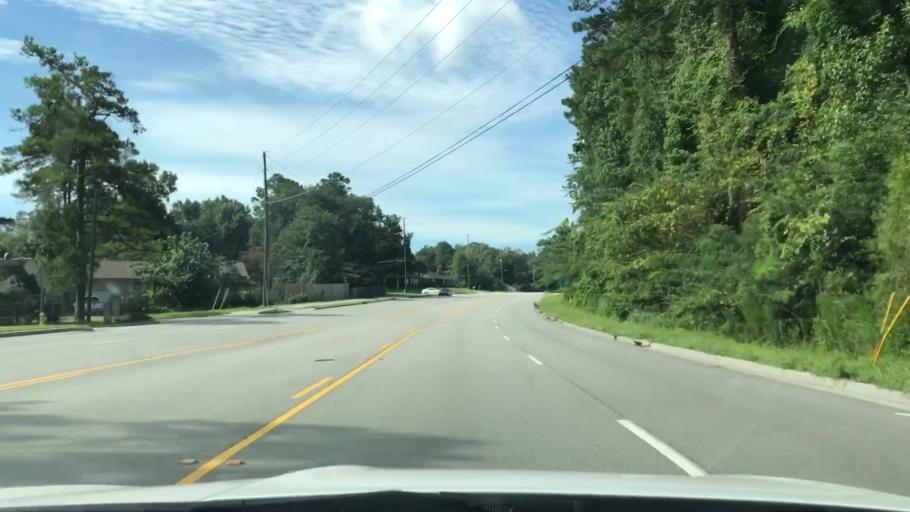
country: US
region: South Carolina
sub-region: Dorchester County
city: Centerville
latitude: 32.9723
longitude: -80.1986
